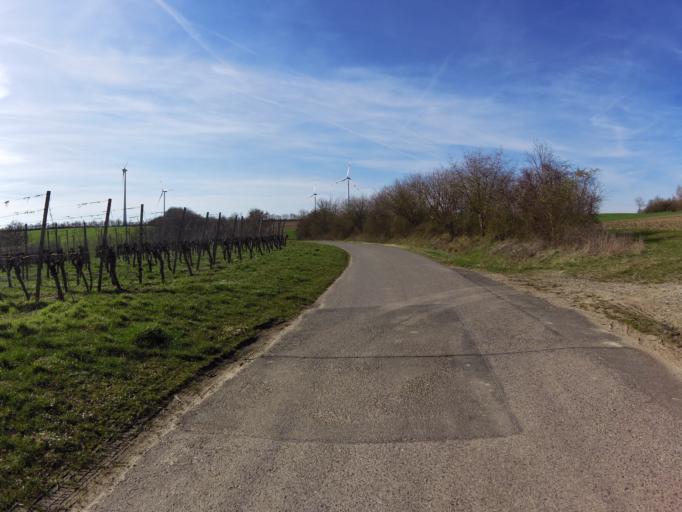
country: DE
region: Bavaria
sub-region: Regierungsbezirk Unterfranken
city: Buchbrunn
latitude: 49.7529
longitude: 10.1155
